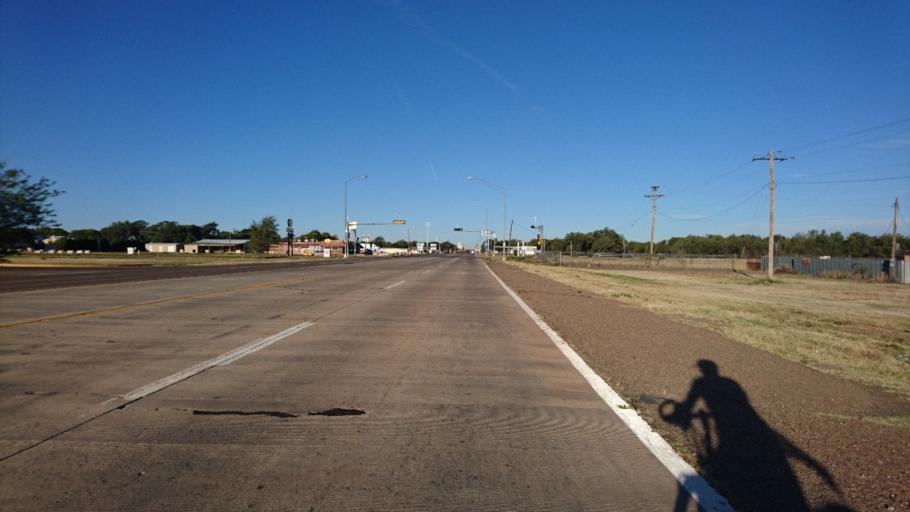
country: US
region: New Mexico
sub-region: Quay County
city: Tucumcari
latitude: 35.1719
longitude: -103.7010
